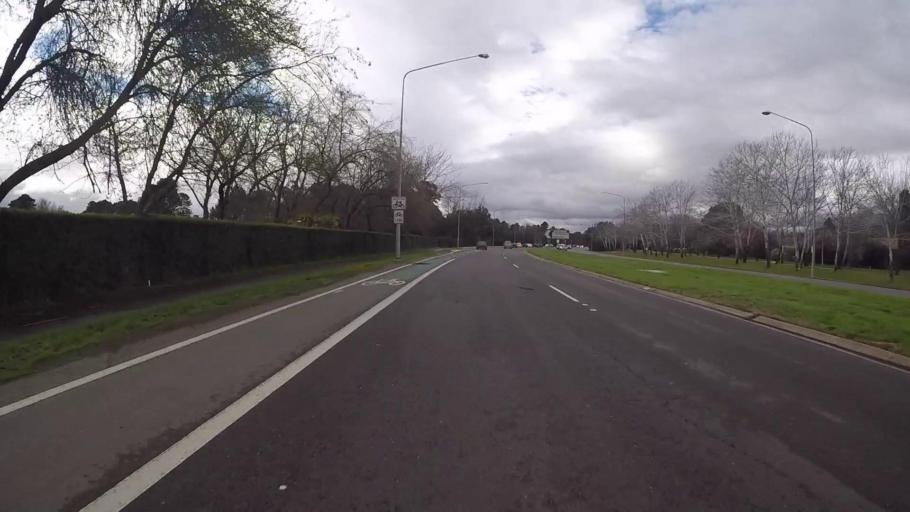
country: AU
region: Australian Capital Territory
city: Kaleen
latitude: -35.2422
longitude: 149.1352
